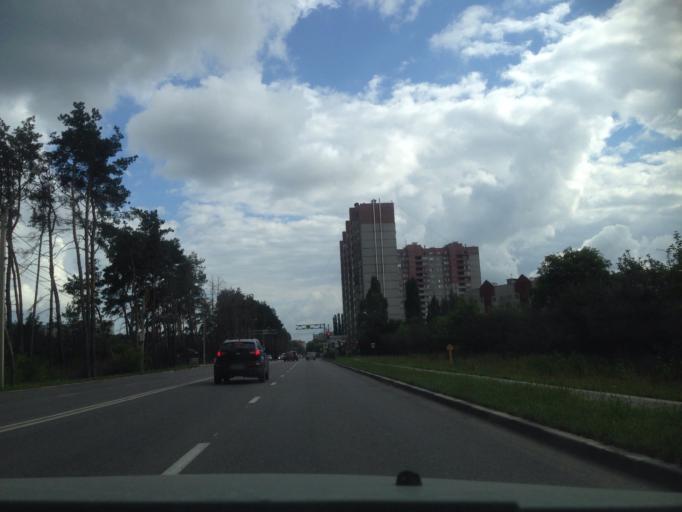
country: RU
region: Voronezj
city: Podgornoye
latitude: 51.7264
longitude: 39.1857
